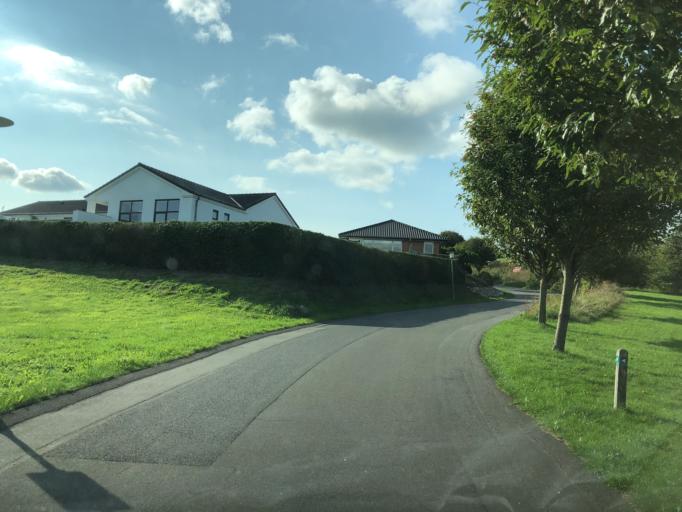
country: DK
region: North Denmark
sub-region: Mariagerfjord Kommune
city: Hobro
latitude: 56.5947
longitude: 9.6317
